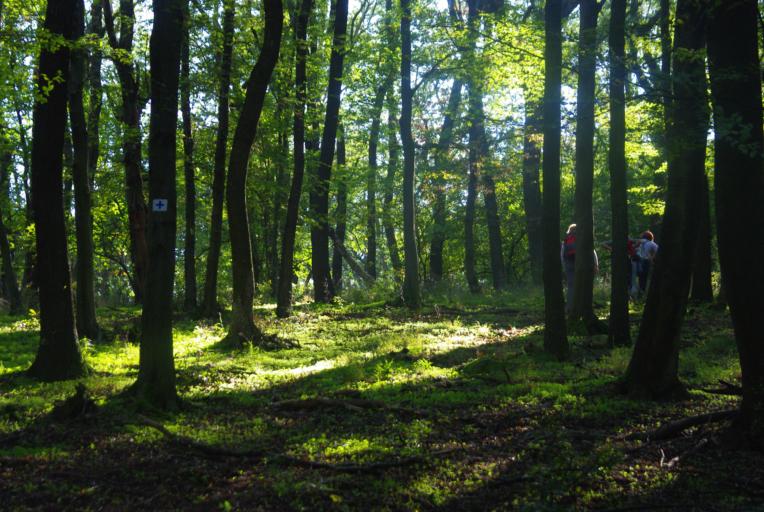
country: HU
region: Pest
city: Szob
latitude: 47.8993
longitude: 18.8323
